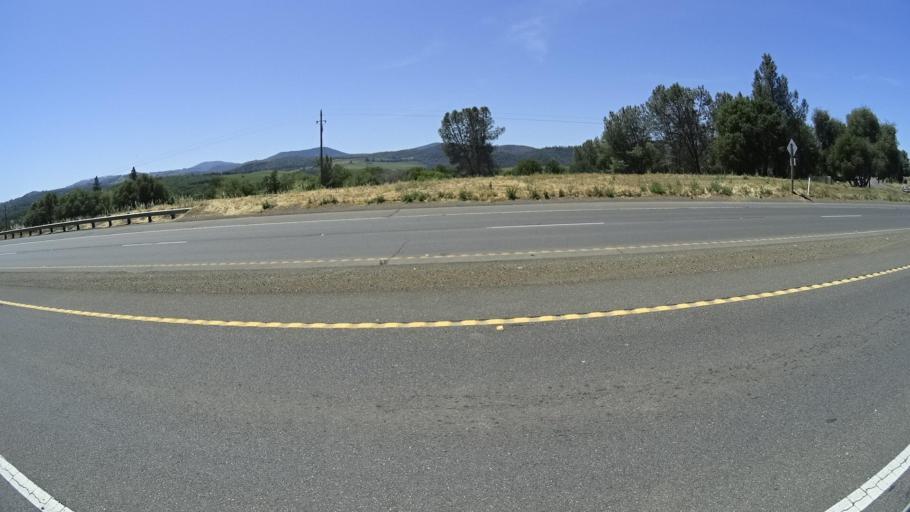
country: US
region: California
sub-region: Lake County
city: Lower Lake
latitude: 38.9294
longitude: -122.6186
